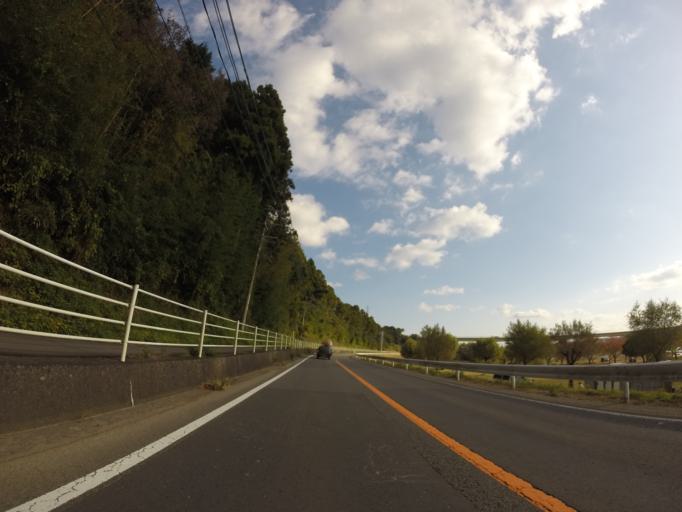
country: JP
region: Shizuoka
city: Kanaya
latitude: 34.8605
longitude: 138.1326
